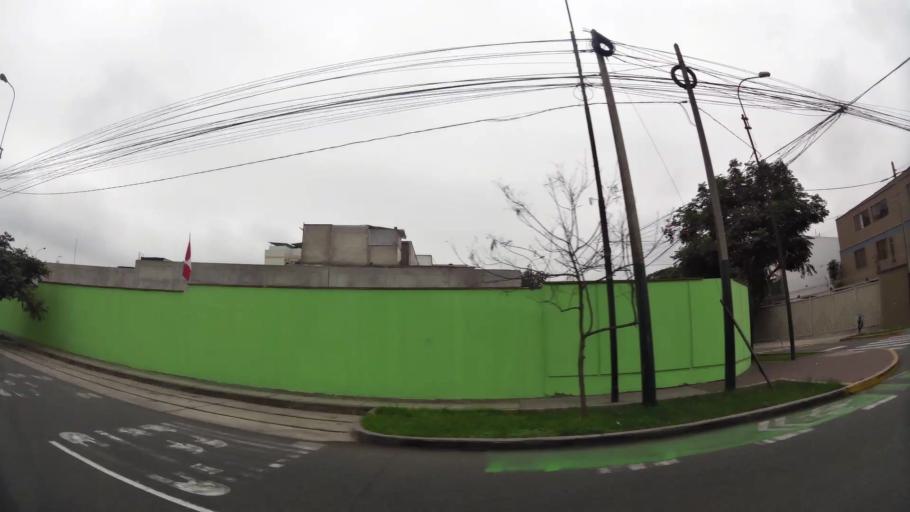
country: PE
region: Lima
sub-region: Lima
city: San Luis
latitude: -12.0917
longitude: -77.0131
